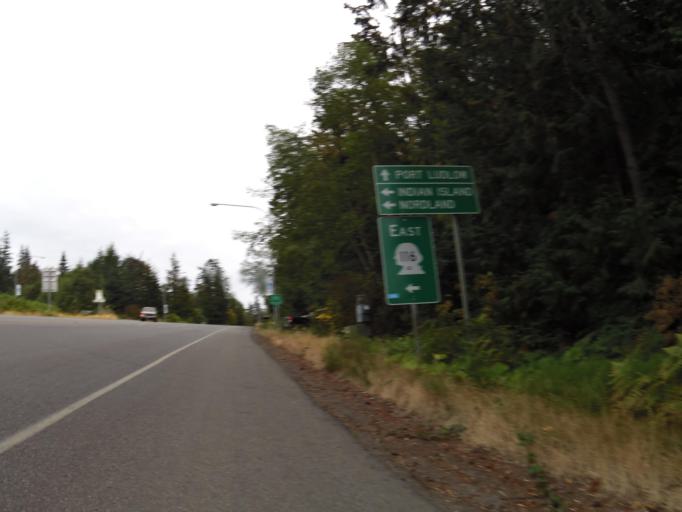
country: US
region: Washington
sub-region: Jefferson County
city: Port Hadlock-Irondale
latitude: 48.0251
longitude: -122.7450
